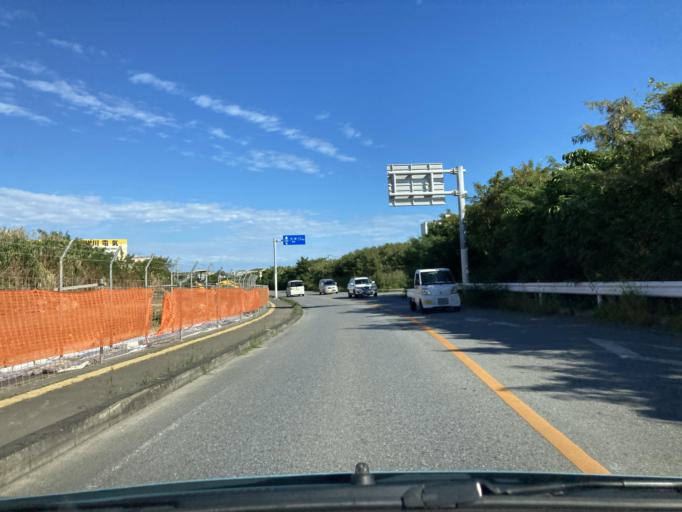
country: JP
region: Okinawa
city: Okinawa
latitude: 26.3712
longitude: 127.7462
